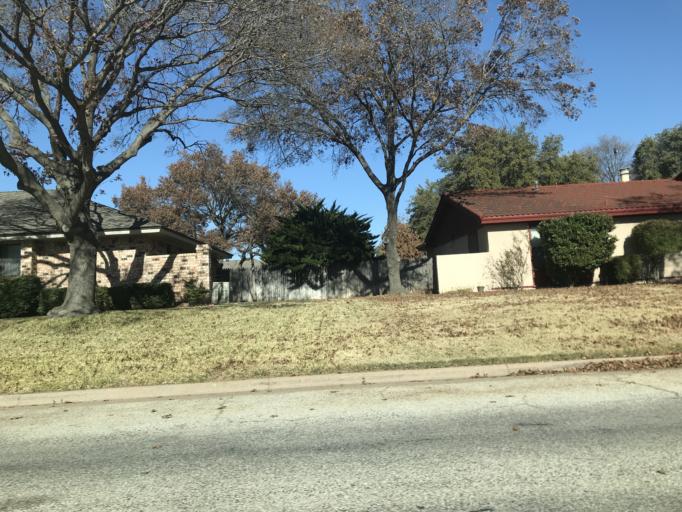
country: US
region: Texas
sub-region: Taylor County
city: Abilene
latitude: 32.3828
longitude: -99.7663
